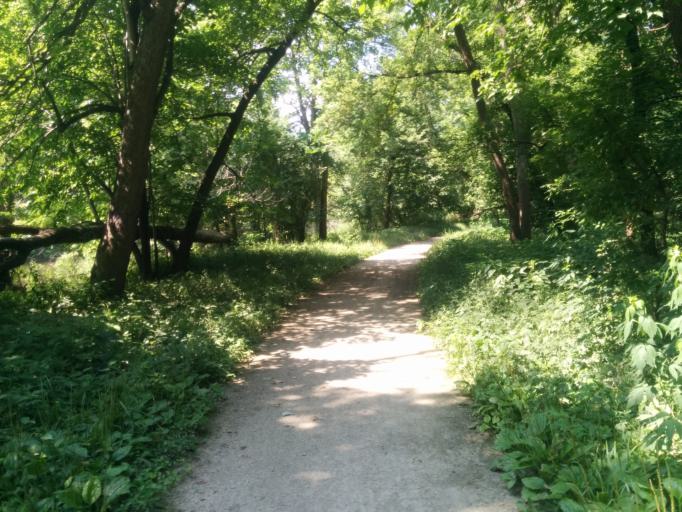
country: US
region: Illinois
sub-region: Cook County
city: River Grove
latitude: 41.9120
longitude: -87.8333
